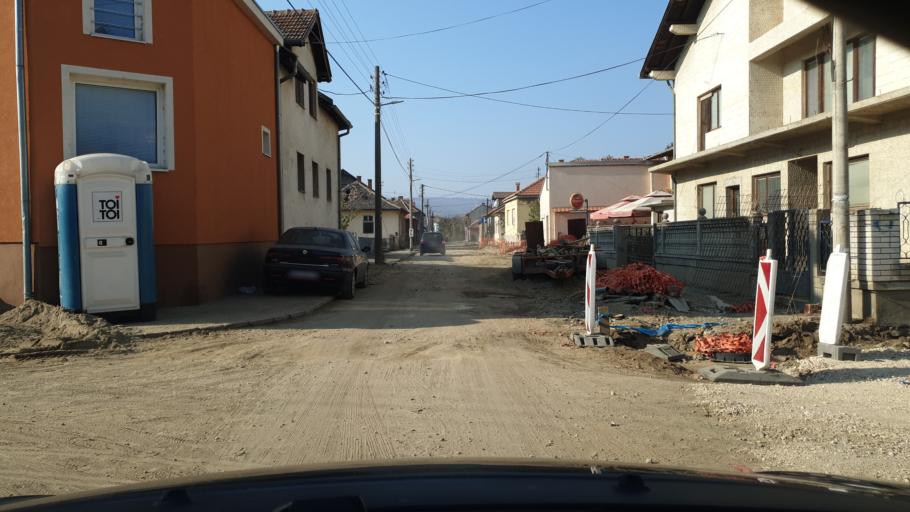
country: RS
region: Central Serbia
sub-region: Borski Okrug
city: Negotin
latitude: 44.2250
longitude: 22.5295
